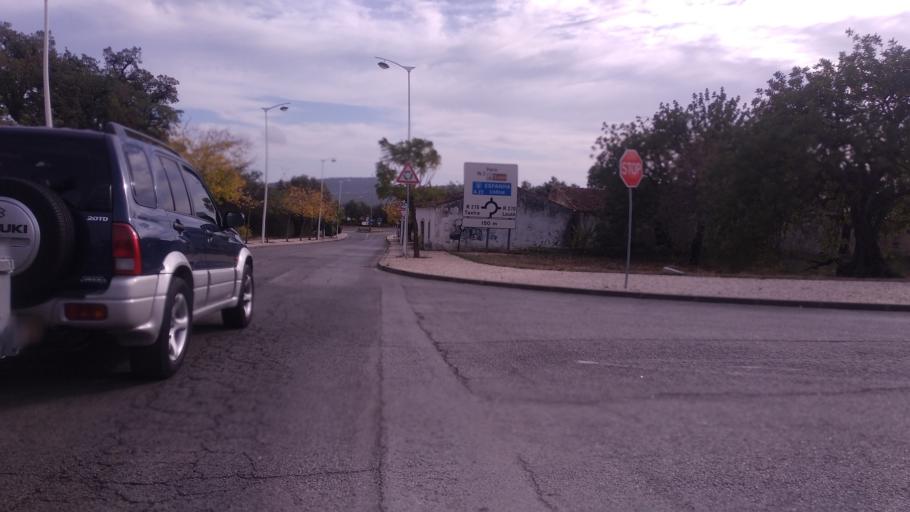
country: PT
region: Faro
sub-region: Sao Bras de Alportel
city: Sao Bras de Alportel
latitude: 37.1484
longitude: -7.8931
